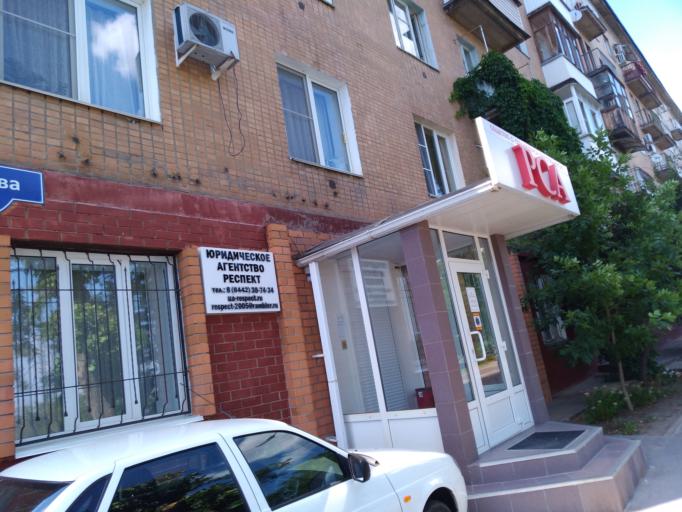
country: RU
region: Volgograd
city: Volgograd
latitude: 48.7101
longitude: 44.5287
